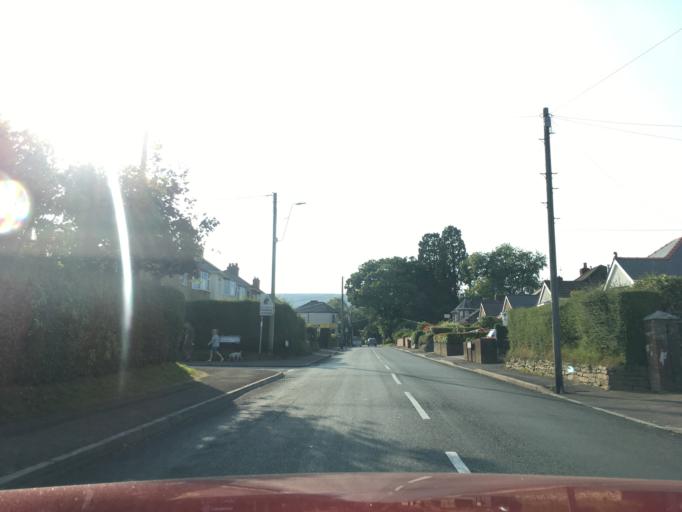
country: GB
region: Wales
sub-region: Torfaen County Borough
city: Cwmbran
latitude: 51.6666
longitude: -3.0277
